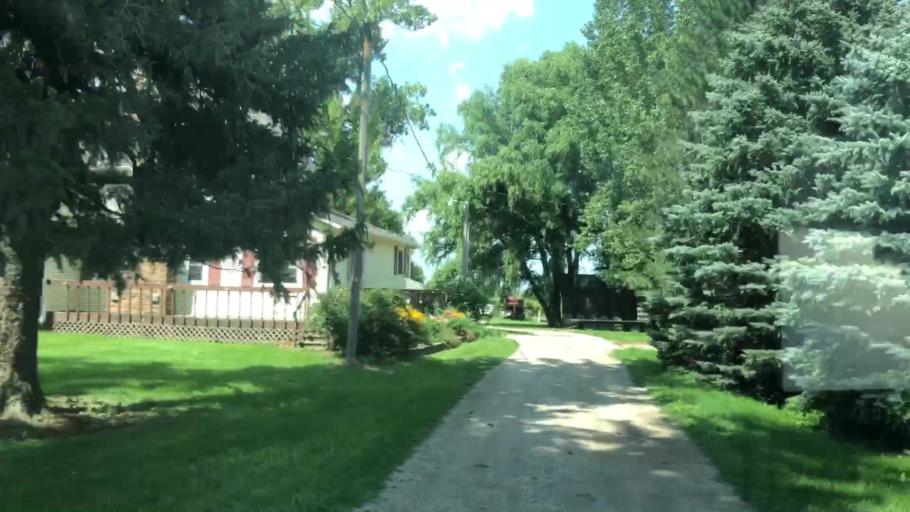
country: US
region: Iowa
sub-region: O'Brien County
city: Sheldon
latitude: 43.1569
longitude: -95.7852
